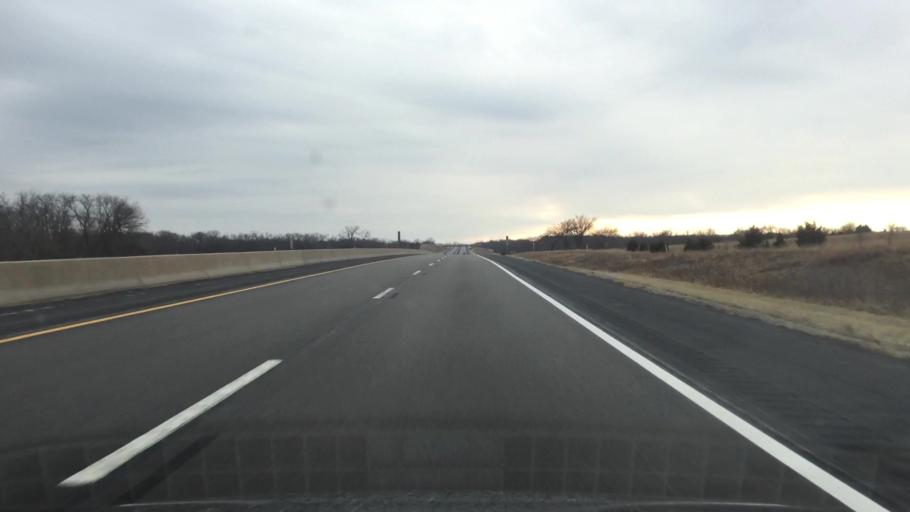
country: US
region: Kansas
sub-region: Osage County
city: Osage City
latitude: 38.7364
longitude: -95.9552
